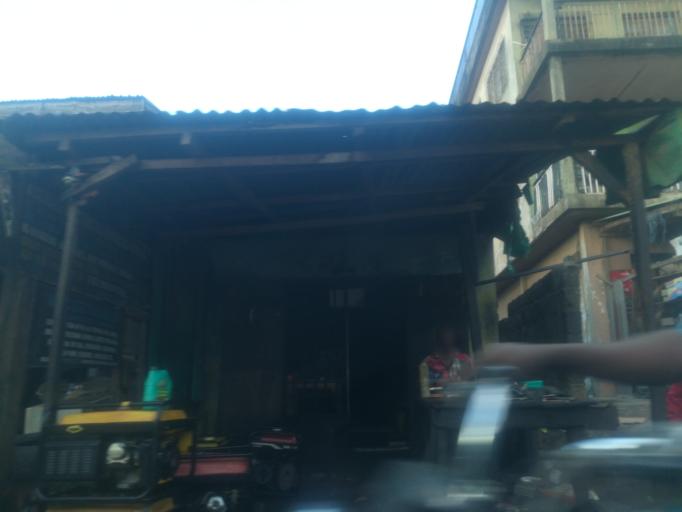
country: NG
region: Oyo
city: Ibadan
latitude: 7.4080
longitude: 3.9472
